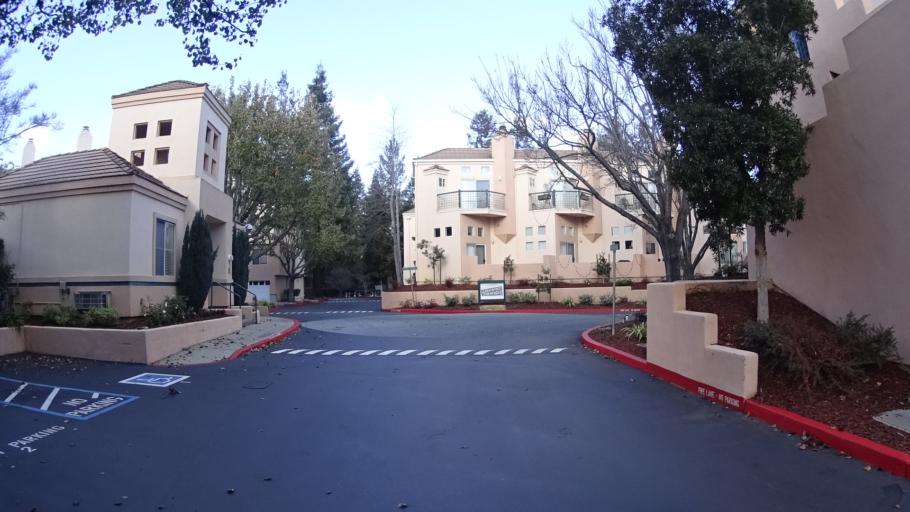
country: US
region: California
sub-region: Santa Clara County
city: Sunnyvale
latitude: 37.3828
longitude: -122.0414
